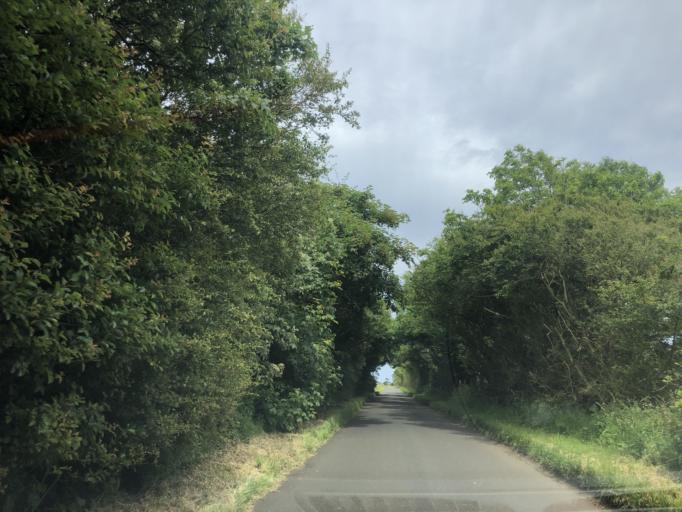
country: GB
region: Scotland
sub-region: Fife
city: Anstruther
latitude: 56.2743
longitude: -2.6100
